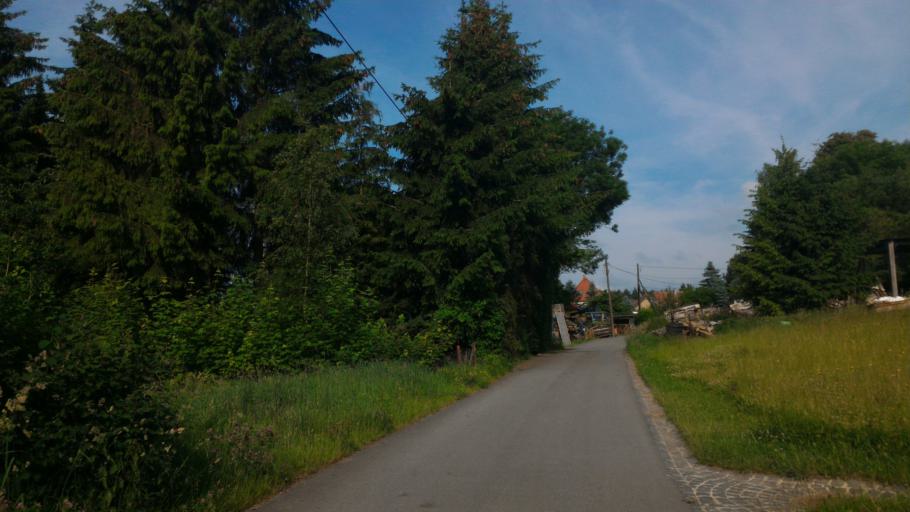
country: DE
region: Saxony
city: Neugersdorf
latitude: 50.9672
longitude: 14.6038
